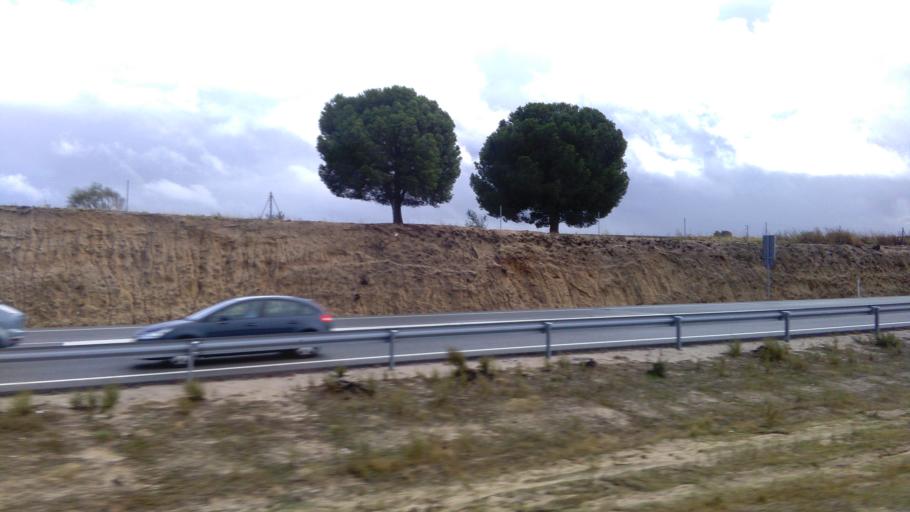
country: ES
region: Castille-La Mancha
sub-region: Province of Toledo
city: Valmojado
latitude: 40.2047
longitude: -4.1029
